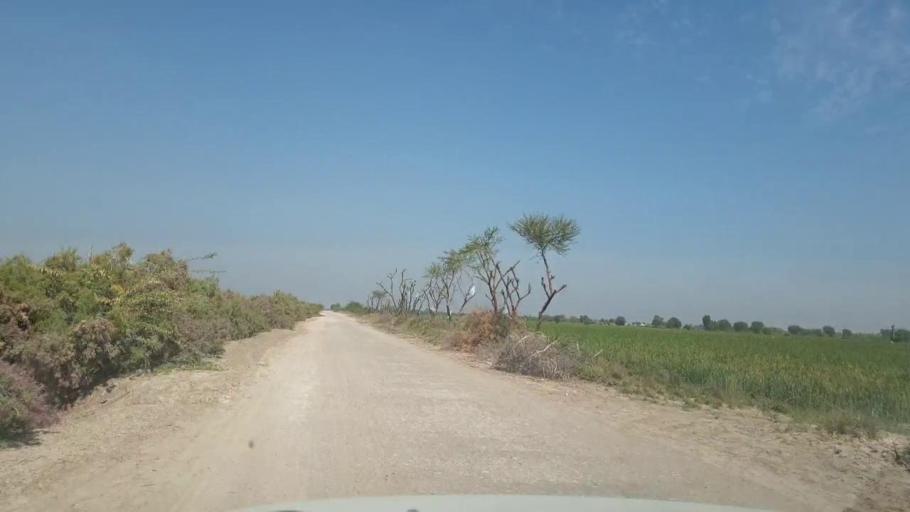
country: PK
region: Sindh
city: Mirpur Khas
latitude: 25.5901
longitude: 69.2010
